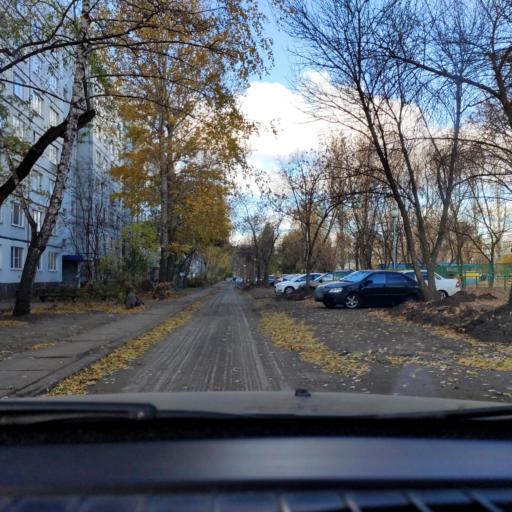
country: RU
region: Samara
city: Tol'yatti
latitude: 53.5302
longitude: 49.2901
